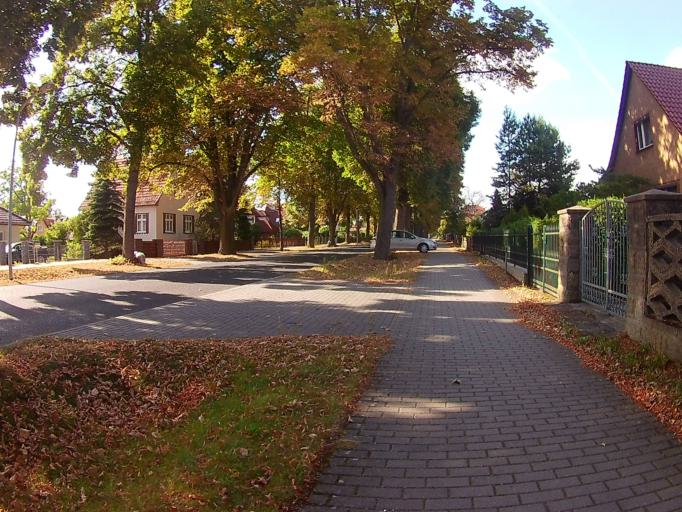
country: DE
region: Brandenburg
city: Zeuthen
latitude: 52.3677
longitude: 13.6072
